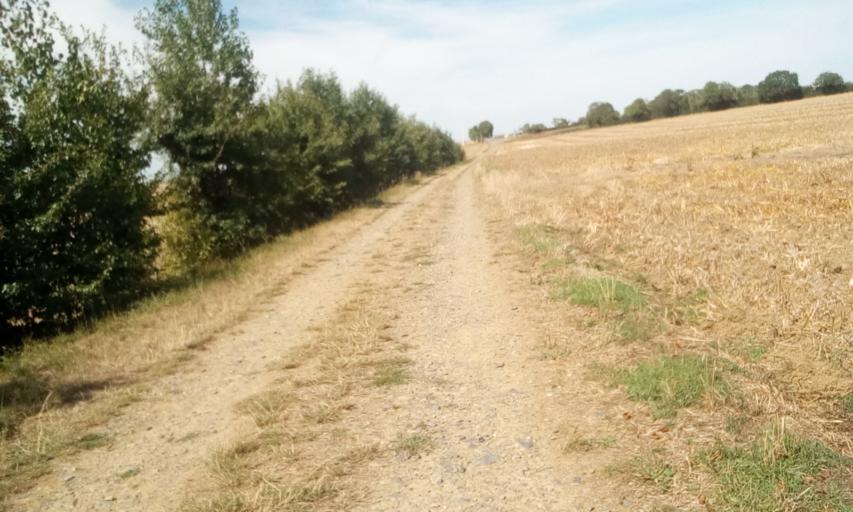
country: FR
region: Lower Normandy
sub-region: Departement du Calvados
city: Fontaine-Etoupefour
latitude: 49.1197
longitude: -0.4592
